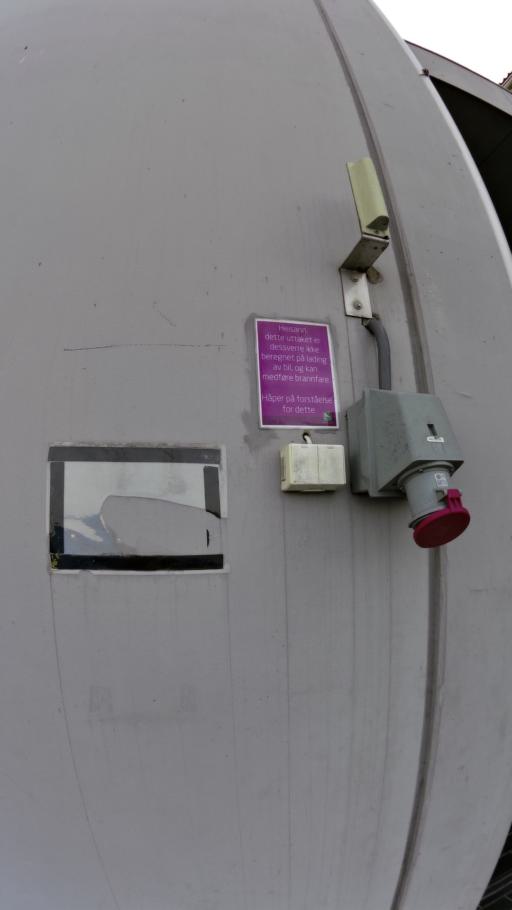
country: NO
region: Ostfold
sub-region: Sarpsborg
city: Sarpsborg
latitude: 59.2971
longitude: 11.0647
